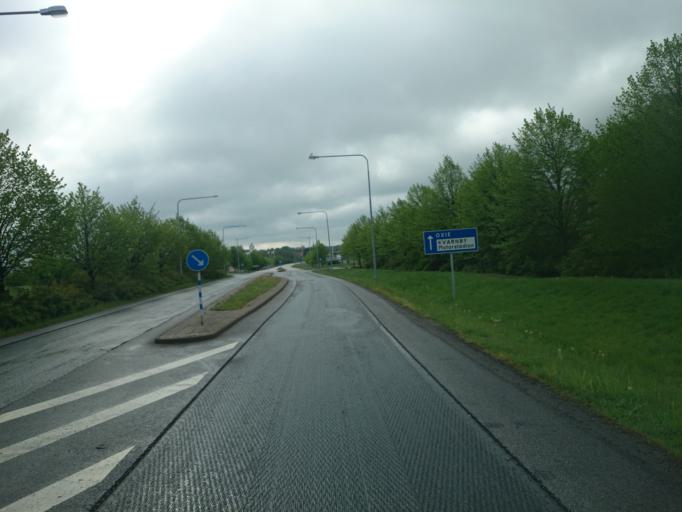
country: SE
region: Skane
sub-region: Burlovs Kommun
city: Arloev
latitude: 55.5792
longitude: 13.0696
